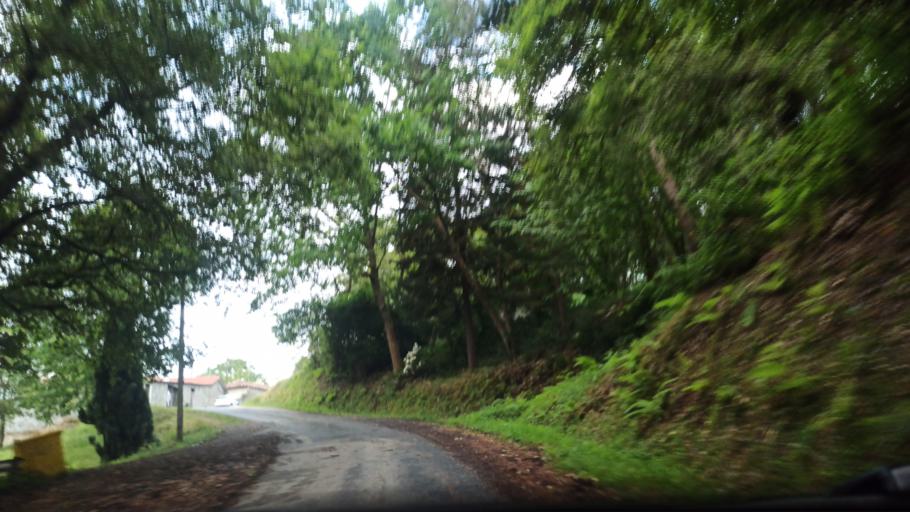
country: ES
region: Galicia
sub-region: Provincia da Coruna
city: Santiso
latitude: 42.8273
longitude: -8.1426
